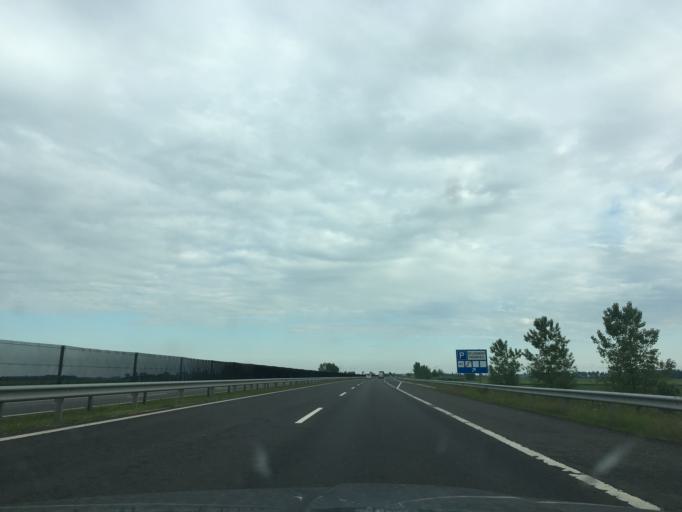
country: HU
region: Hajdu-Bihar
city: Hajduboszormeny
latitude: 47.6964
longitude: 21.4398
